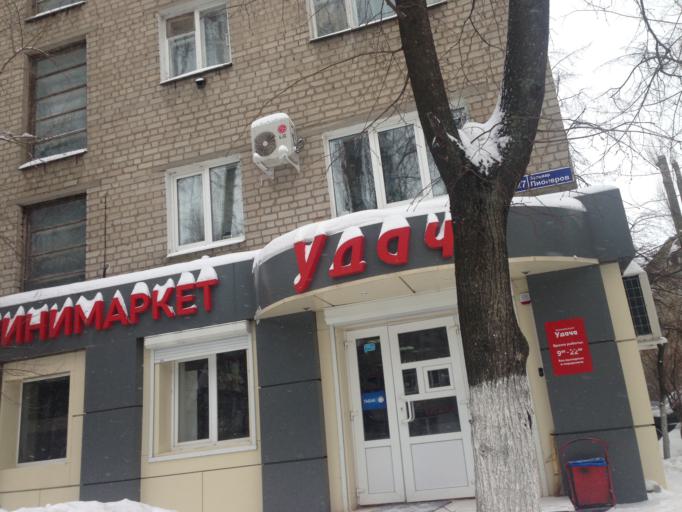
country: RU
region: Voronezj
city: Voronezh
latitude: 51.6545
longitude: 39.1490
